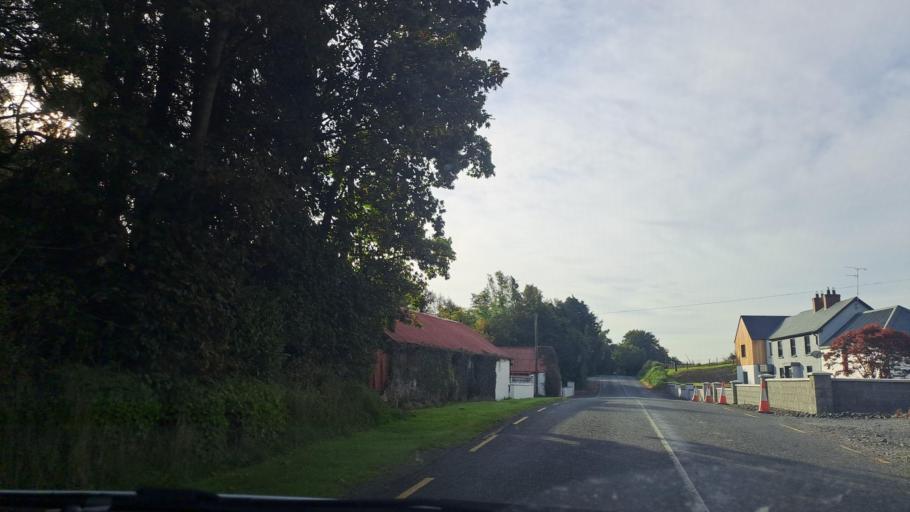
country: IE
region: Ulster
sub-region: An Cabhan
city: Kingscourt
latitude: 53.9513
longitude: -6.8405
